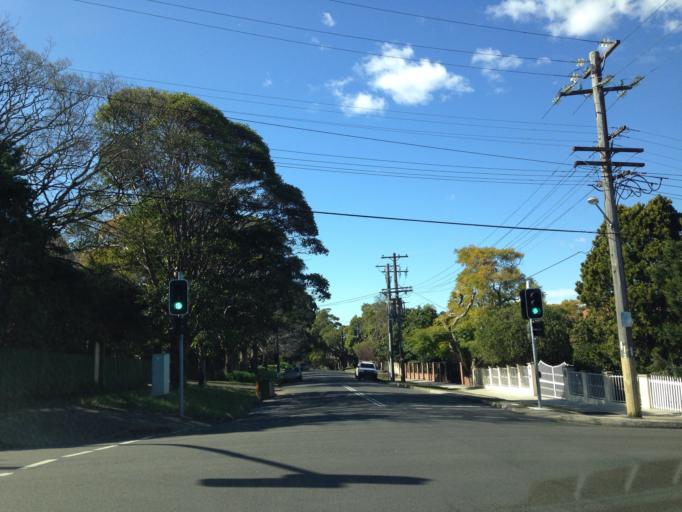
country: AU
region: New South Wales
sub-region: Ku-ring-gai
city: Killara
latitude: -33.7629
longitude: 151.1601
